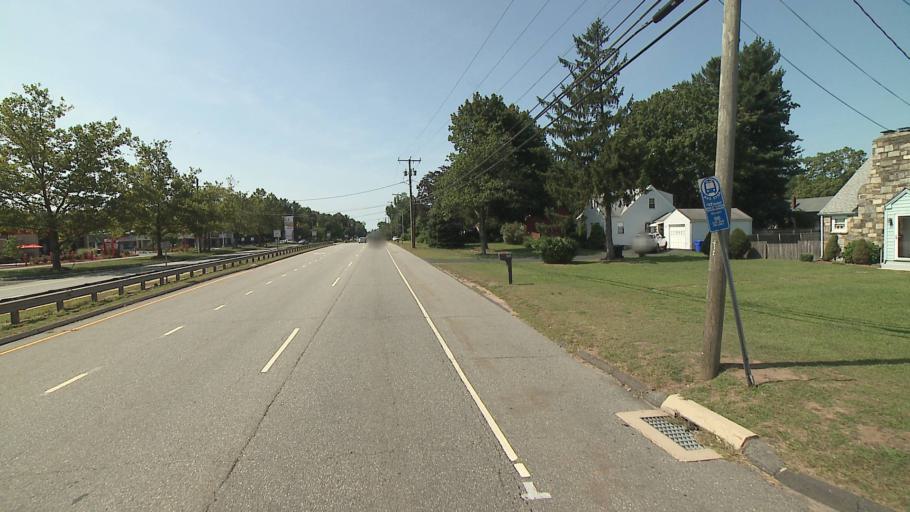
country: US
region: Connecticut
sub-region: Hartford County
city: East Hartford
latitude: 41.7959
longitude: -72.6215
